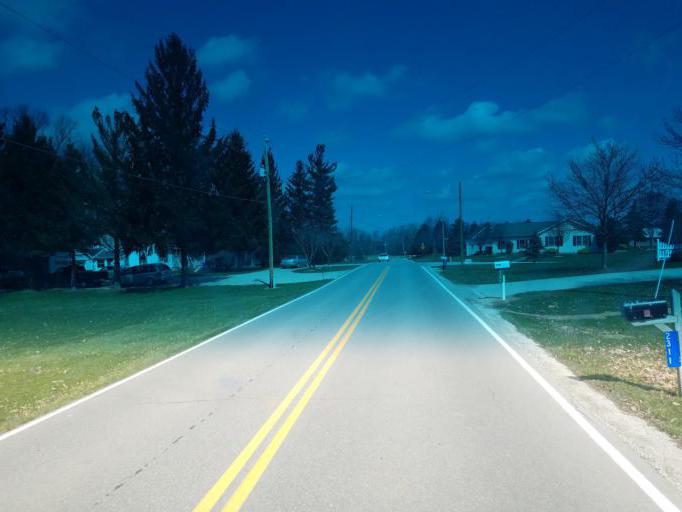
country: US
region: Ohio
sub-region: Crawford County
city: Bucyrus
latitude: 40.8001
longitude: -83.0024
